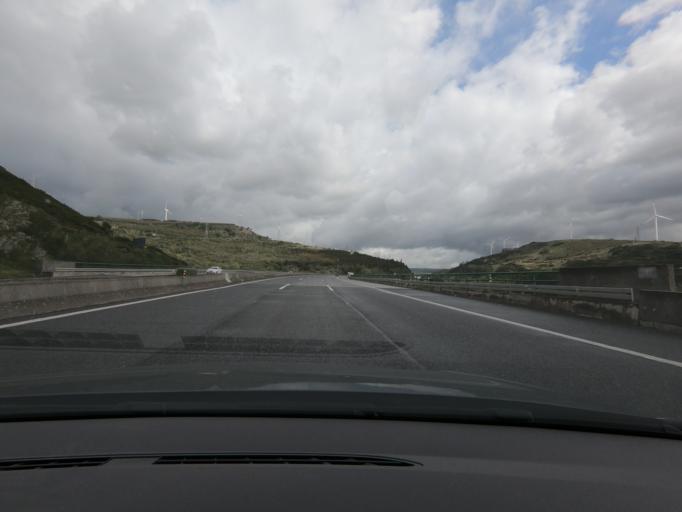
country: PT
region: Lisbon
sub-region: Loures
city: Santo Antao do Tojal
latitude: 38.8725
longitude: -9.1346
